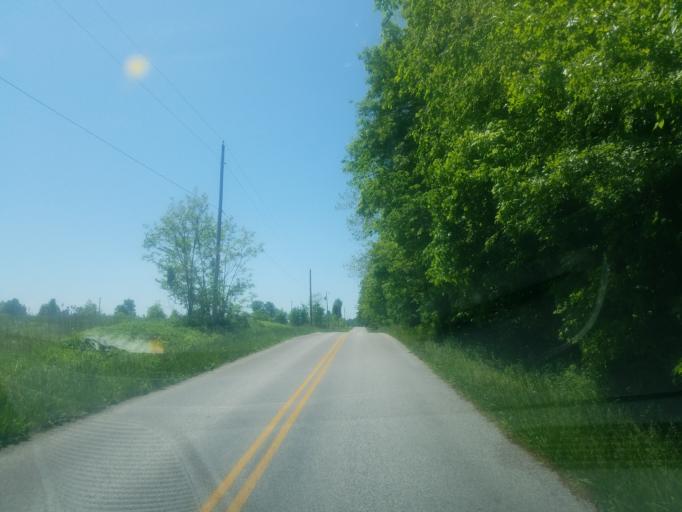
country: US
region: Ohio
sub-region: Huron County
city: Wakeman
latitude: 41.1706
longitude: -82.3756
